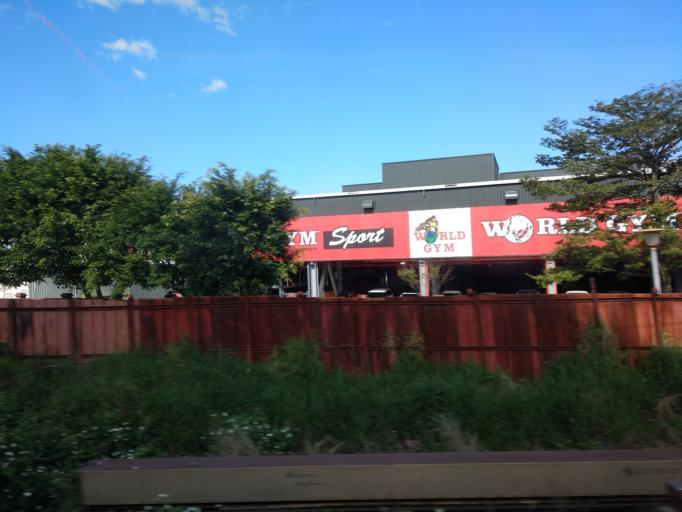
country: TW
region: Taiwan
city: Taoyuan City
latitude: 24.9683
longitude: 121.2506
